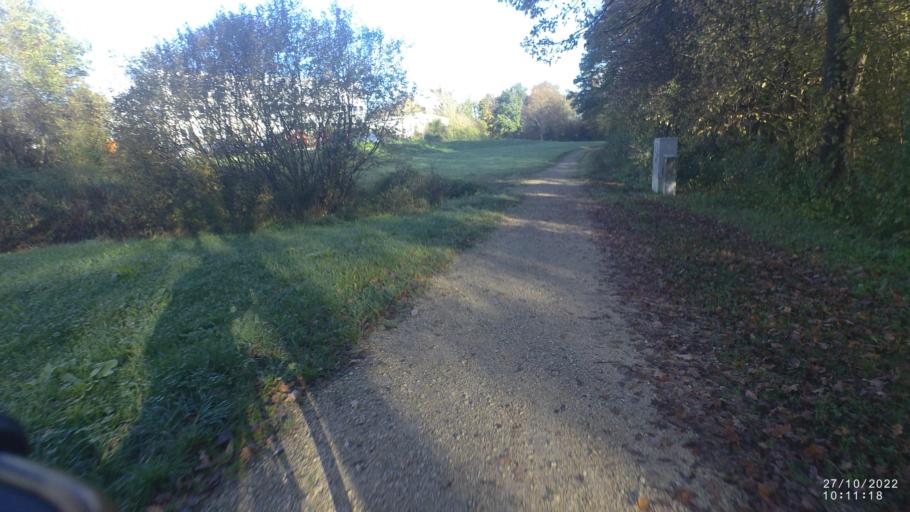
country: DE
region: Baden-Wuerttemberg
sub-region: Regierungsbezirk Stuttgart
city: Eschenbach
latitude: 48.6662
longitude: 9.6842
